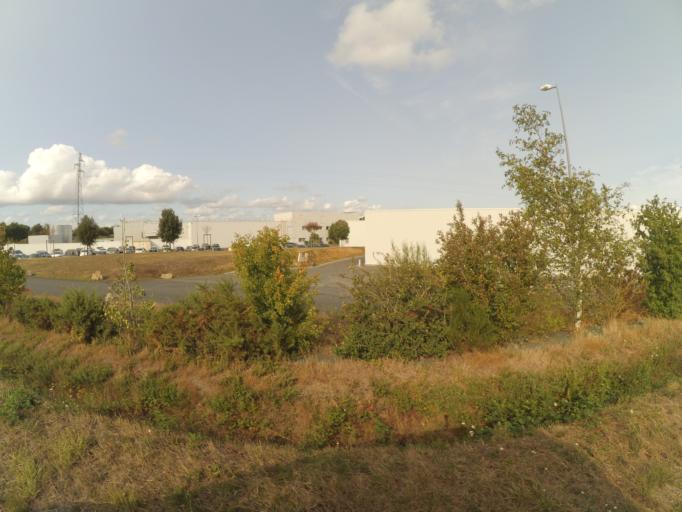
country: FR
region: Pays de la Loire
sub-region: Departement de la Vendee
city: Bouffere
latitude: 46.9700
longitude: -1.3337
